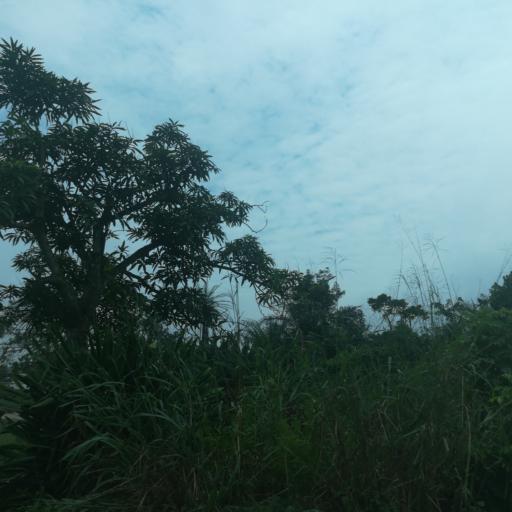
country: NG
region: Lagos
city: Ejirin
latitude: 6.6601
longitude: 3.7943
